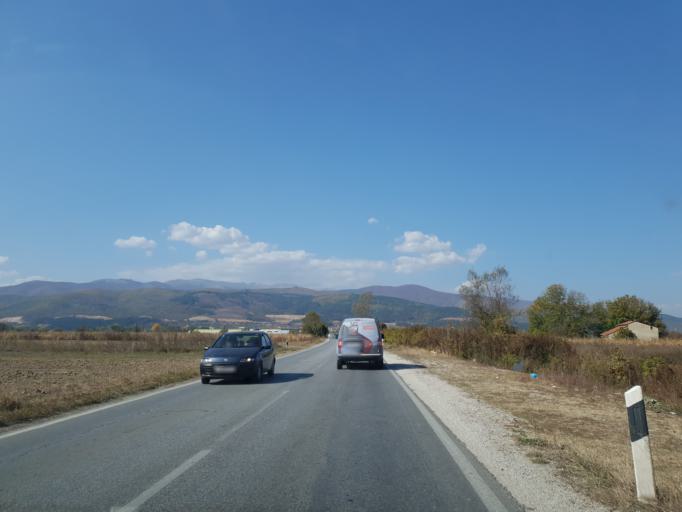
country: MK
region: Kicevo
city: Kicevo
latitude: 41.4865
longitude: 20.9745
